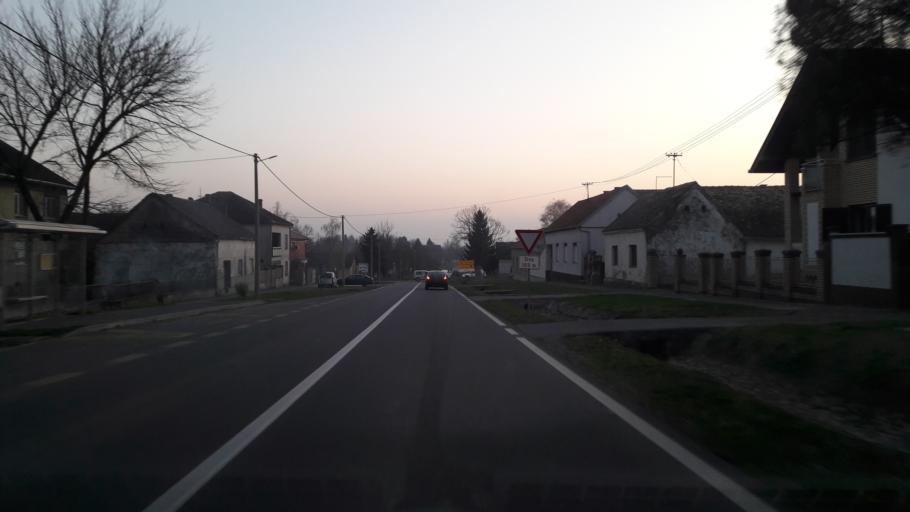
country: HR
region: Vukovarsko-Srijemska
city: Slakovci
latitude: 45.2162
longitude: 18.9851
